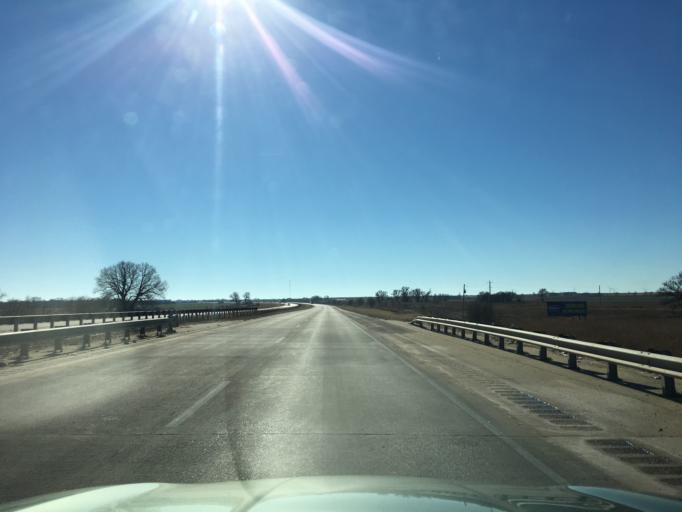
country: US
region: Oklahoma
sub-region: Kay County
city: Blackwell
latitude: 36.9069
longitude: -97.3532
